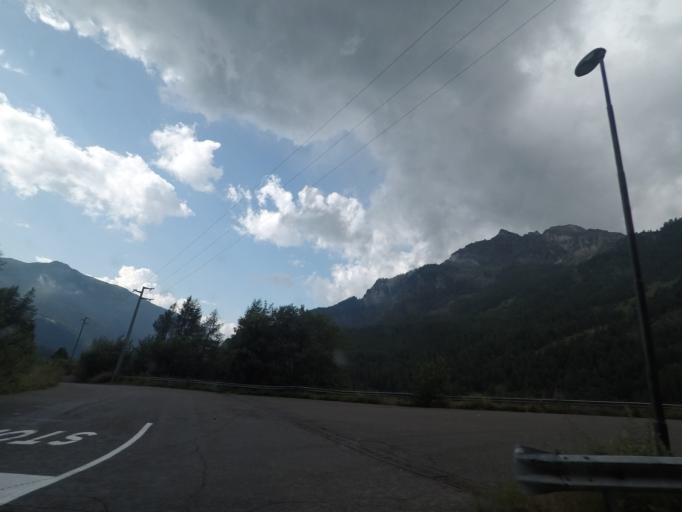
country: IT
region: Aosta Valley
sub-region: Valle d'Aosta
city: Paquier
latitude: 45.8956
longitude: 7.6219
